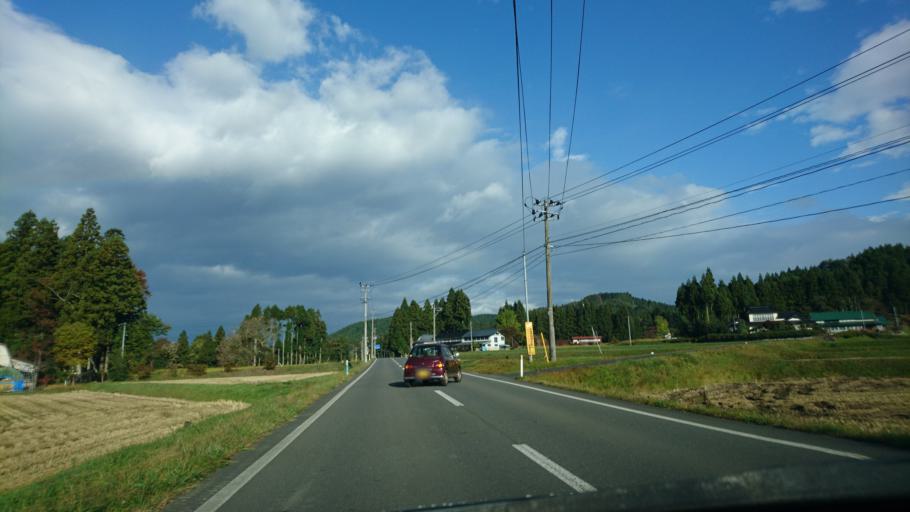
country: JP
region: Iwate
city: Mizusawa
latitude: 39.0515
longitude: 141.0460
